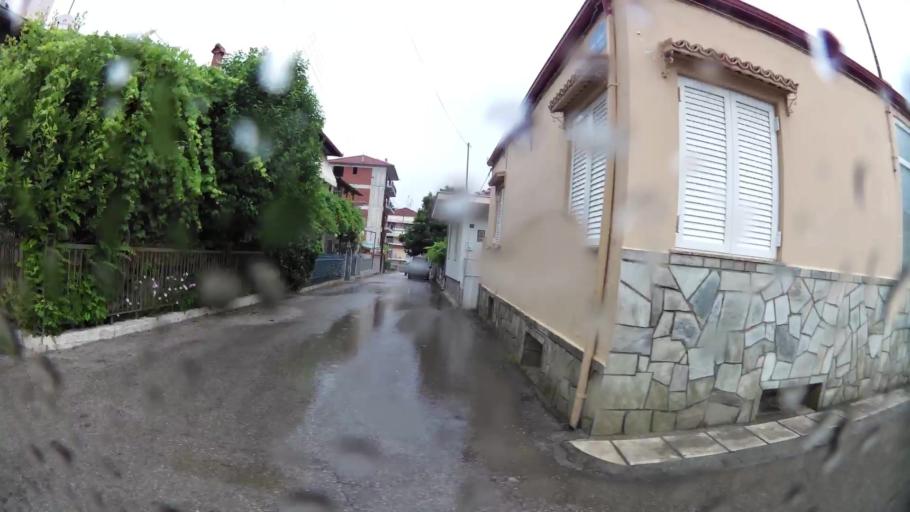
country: GR
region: Central Macedonia
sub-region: Nomos Imathias
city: Veroia
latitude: 40.5333
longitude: 22.2036
